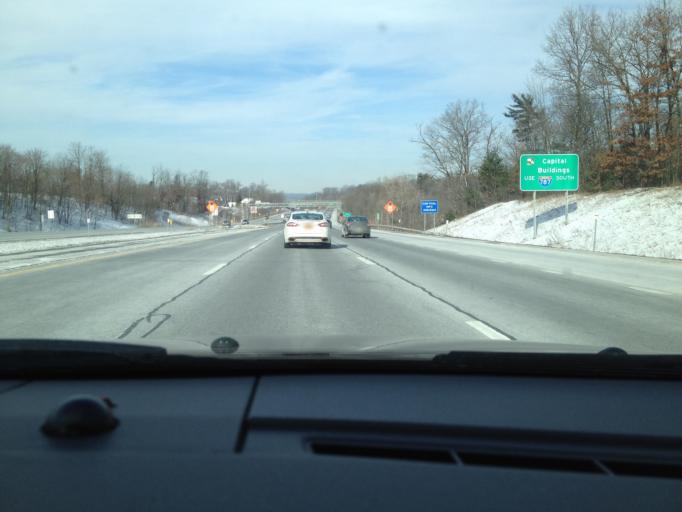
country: US
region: New York
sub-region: Rensselaer County
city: Rensselaer
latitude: 42.6553
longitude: -73.7182
